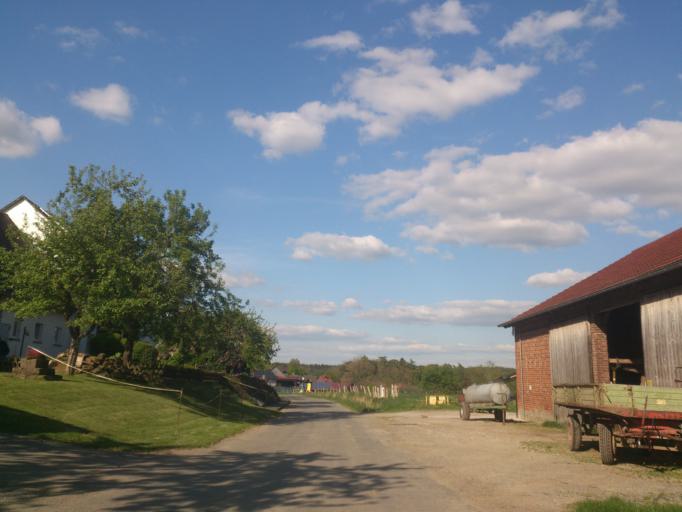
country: DE
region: North Rhine-Westphalia
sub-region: Regierungsbezirk Detmold
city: Willebadessen
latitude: 51.6115
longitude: 9.0717
